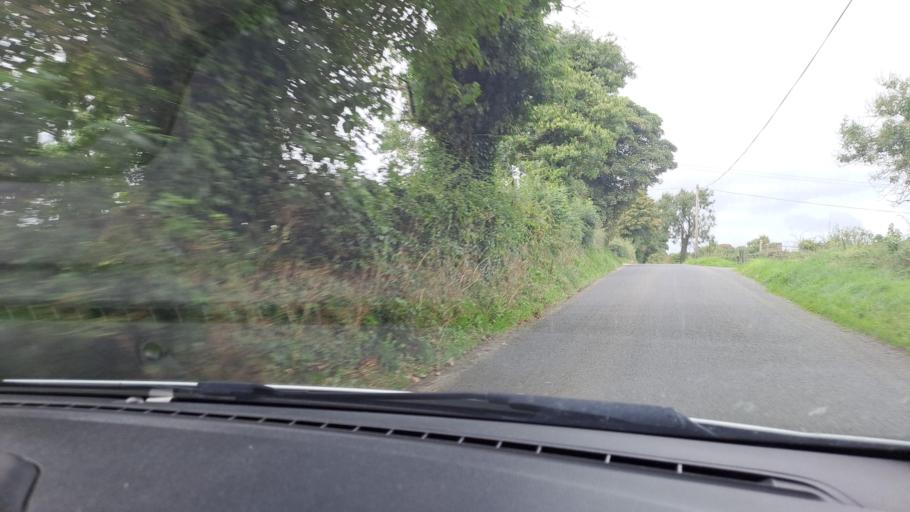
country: IE
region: Ulster
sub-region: County Monaghan
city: Carrickmacross
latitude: 54.0001
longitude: -6.7980
